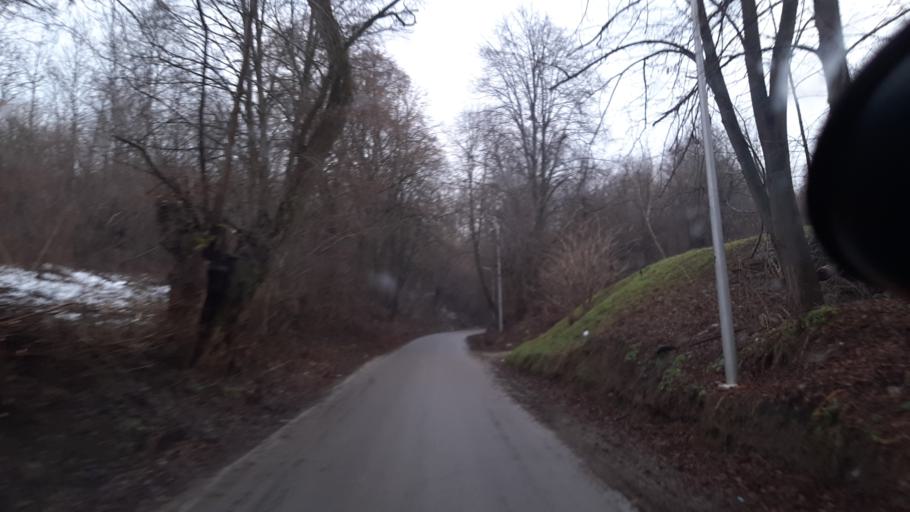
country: PL
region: Lublin Voivodeship
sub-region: Powiat lubelski
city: Lublin
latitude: 51.3156
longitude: 22.5787
